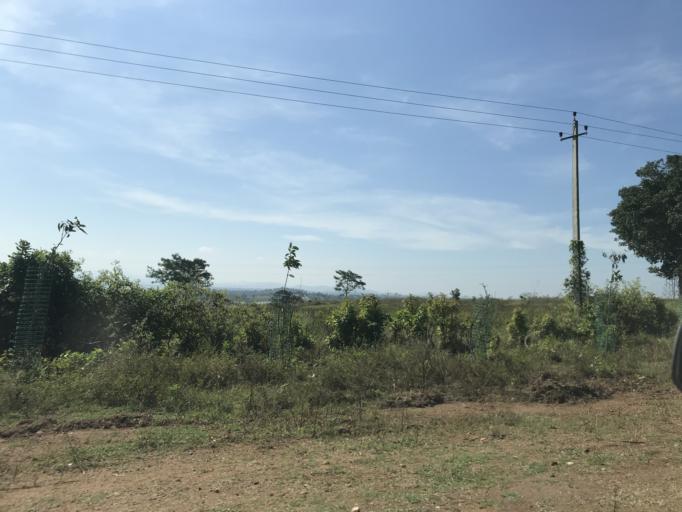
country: IN
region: Karnataka
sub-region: Mysore
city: Heggadadevankote
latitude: 12.0157
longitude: 76.2764
